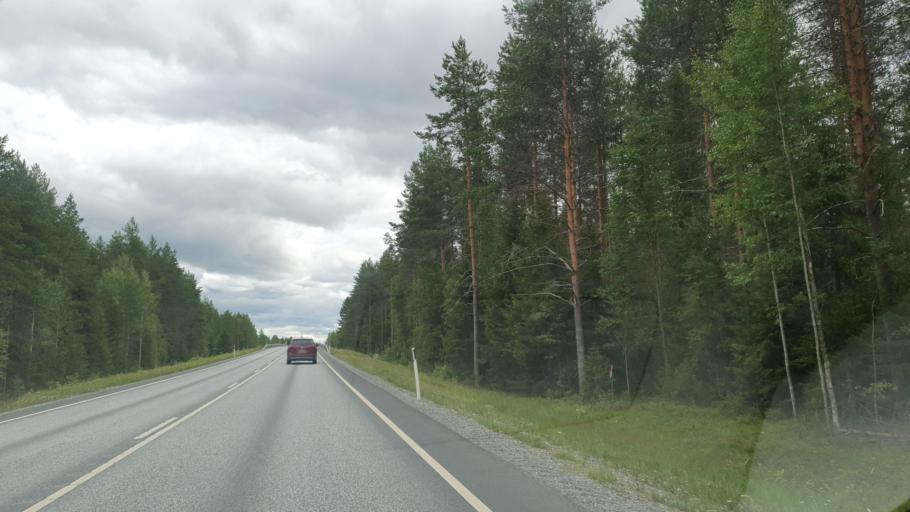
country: FI
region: Northern Savo
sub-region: Ylae-Savo
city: Sonkajaervi
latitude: 63.8899
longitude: 27.4265
